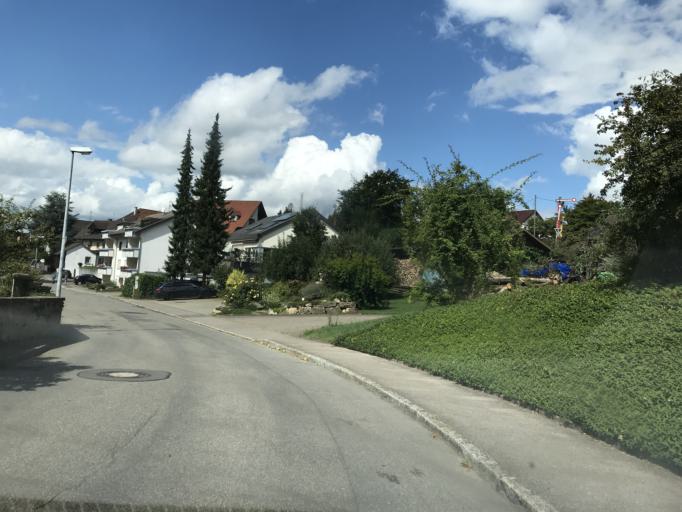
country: DE
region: Baden-Wuerttemberg
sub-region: Freiburg Region
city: Rheinfelden (Baden)
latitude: 47.5998
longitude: 7.7590
